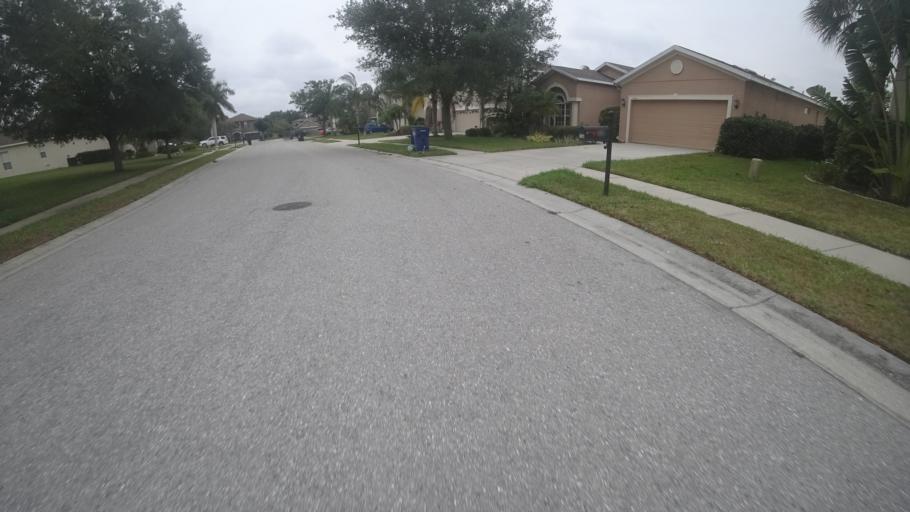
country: US
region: Florida
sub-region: Manatee County
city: Samoset
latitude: 27.4325
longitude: -82.5075
